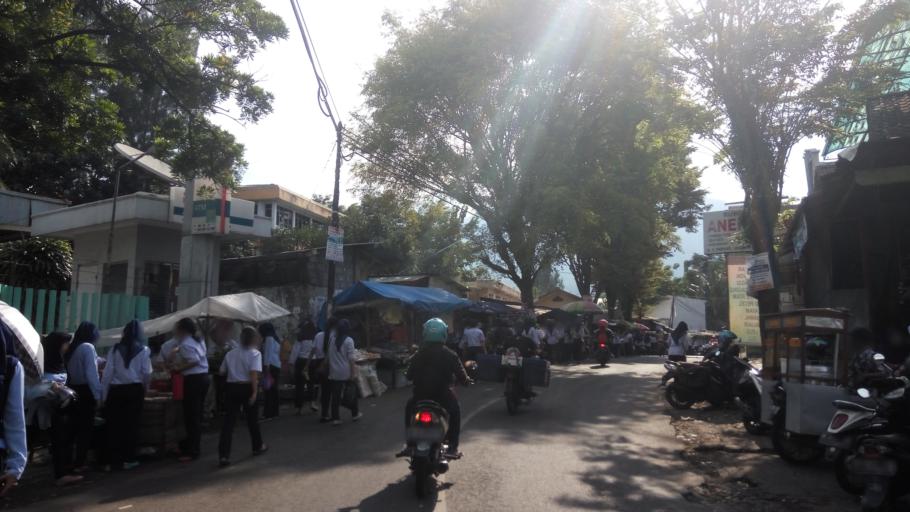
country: ID
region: Central Java
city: Ungaran
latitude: -7.1461
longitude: 110.4091
